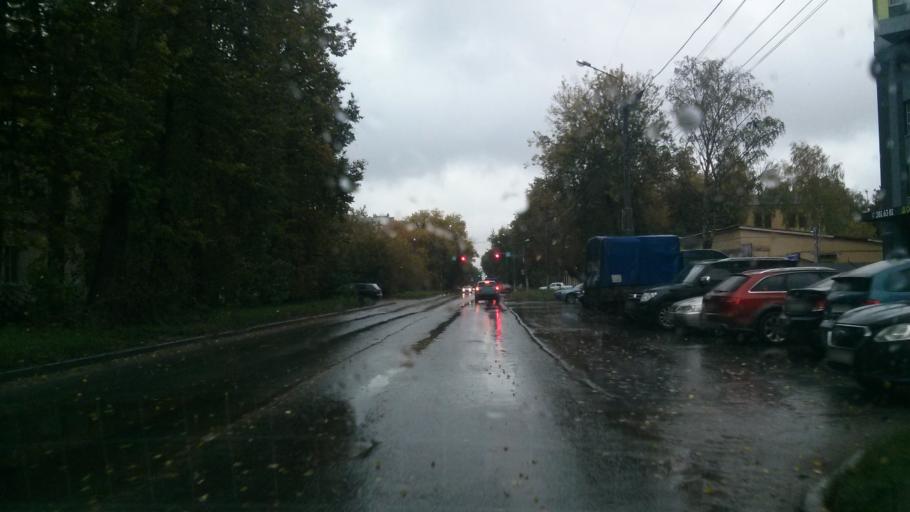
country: RU
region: Nizjnij Novgorod
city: Nizhniy Novgorod
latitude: 56.3107
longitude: 44.0105
